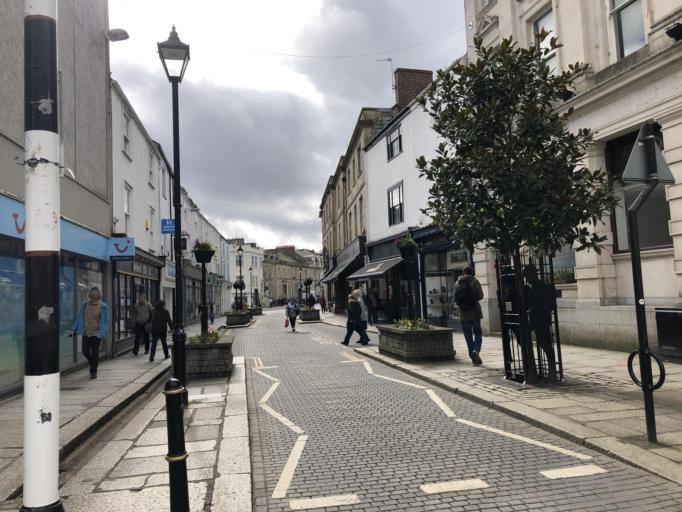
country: GB
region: England
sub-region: Cornwall
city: Truro
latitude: 50.2633
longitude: -5.0510
